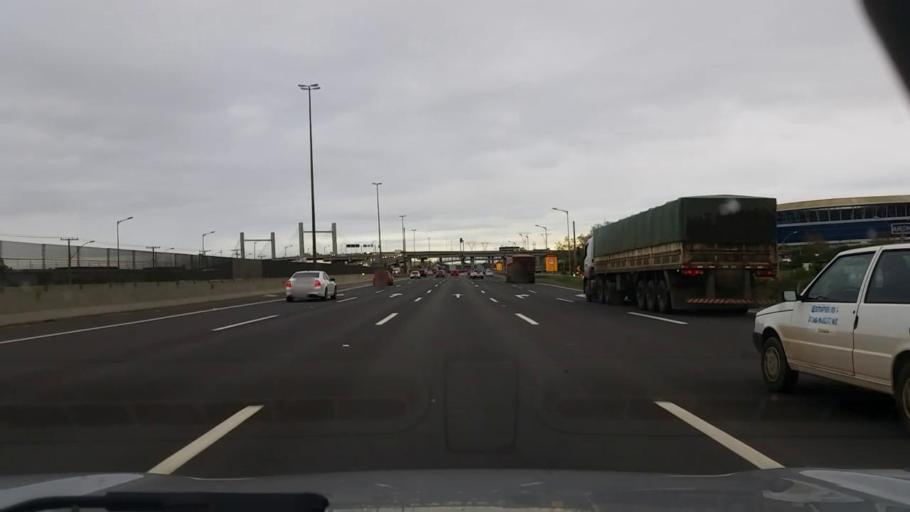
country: BR
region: Rio Grande do Sul
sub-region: Porto Alegre
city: Porto Alegre
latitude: -29.9791
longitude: -51.2004
